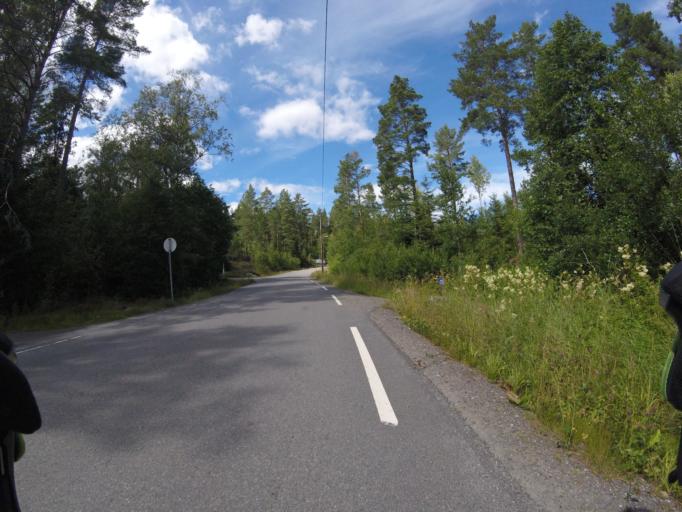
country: NO
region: Akershus
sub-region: Lorenskog
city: Kjenn
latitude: 59.8924
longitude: 10.9767
